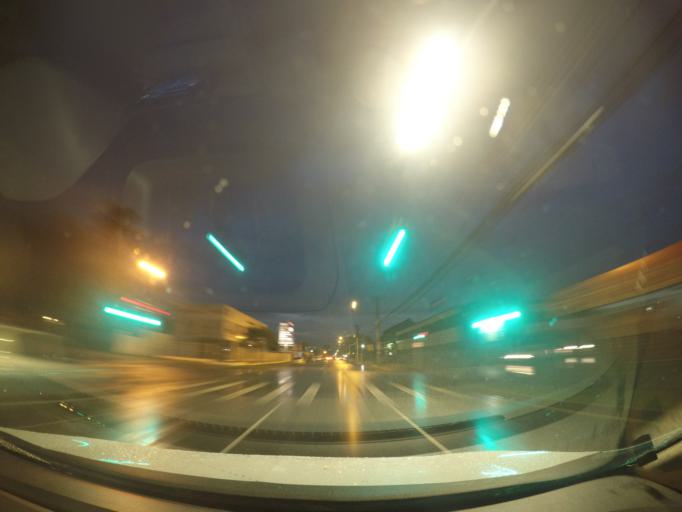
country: BR
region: Parana
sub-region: Curitiba
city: Curitiba
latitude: -25.4824
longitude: -49.2538
